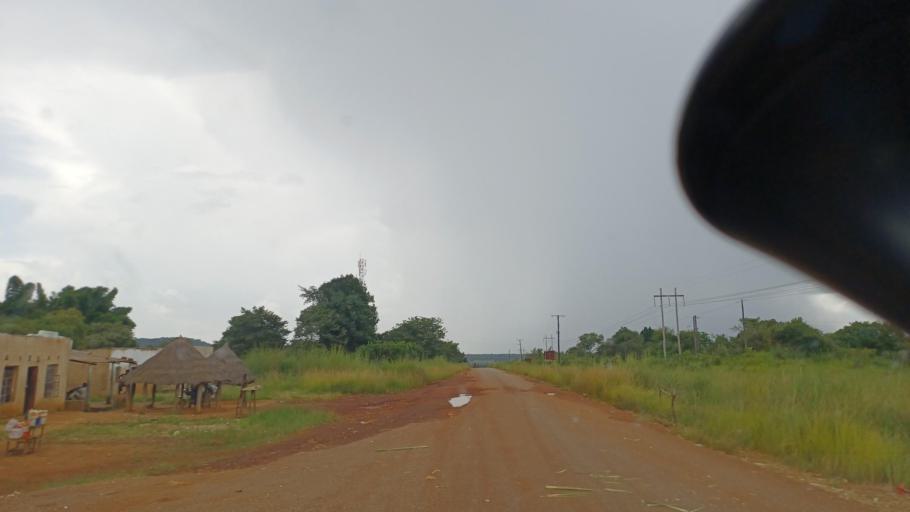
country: ZM
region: North-Western
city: Kasempa
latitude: -13.0546
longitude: 25.9869
